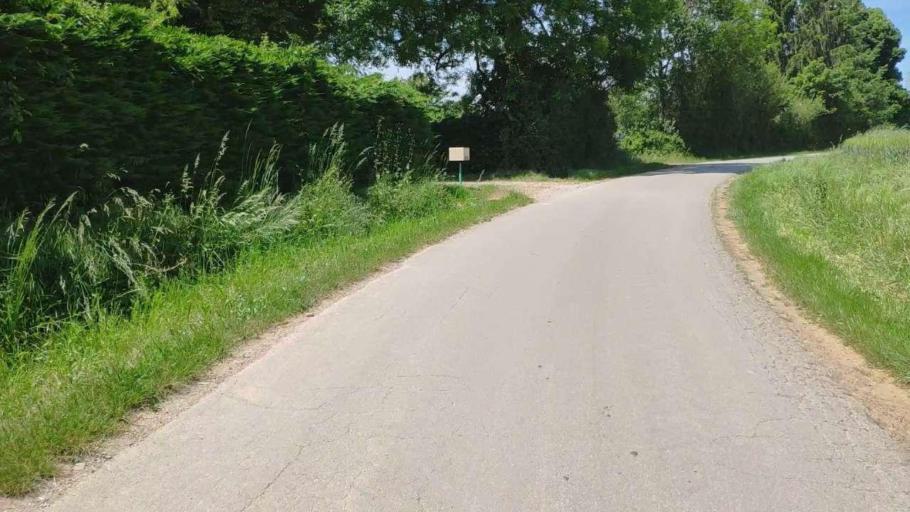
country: FR
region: Franche-Comte
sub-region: Departement du Jura
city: Bletterans
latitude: 46.7813
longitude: 5.3815
